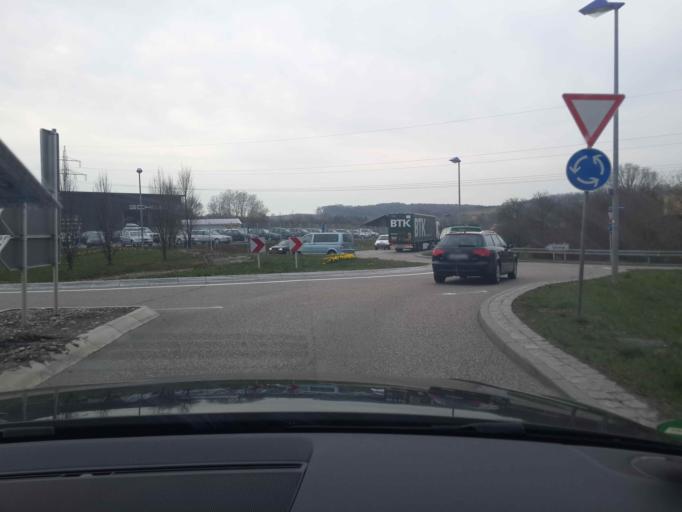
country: DE
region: Baden-Wuerttemberg
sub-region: Regierungsbezirk Stuttgart
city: Ohringen
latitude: 49.2073
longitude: 9.4811
